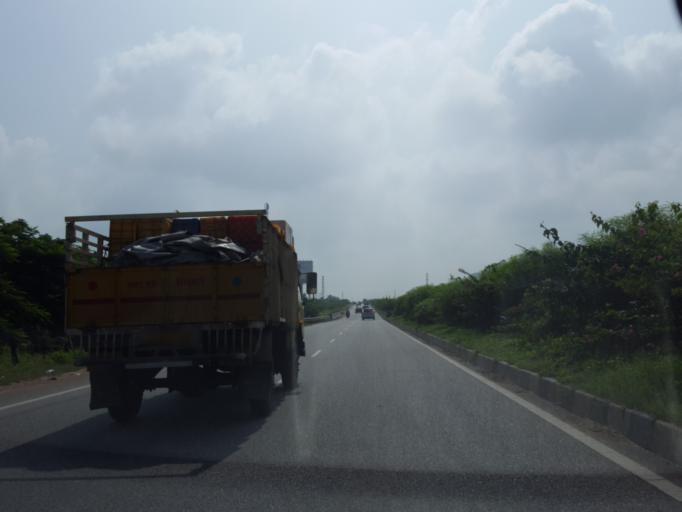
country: IN
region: Telangana
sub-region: Rangareddi
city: Ghatkesar
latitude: 17.2792
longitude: 78.8058
